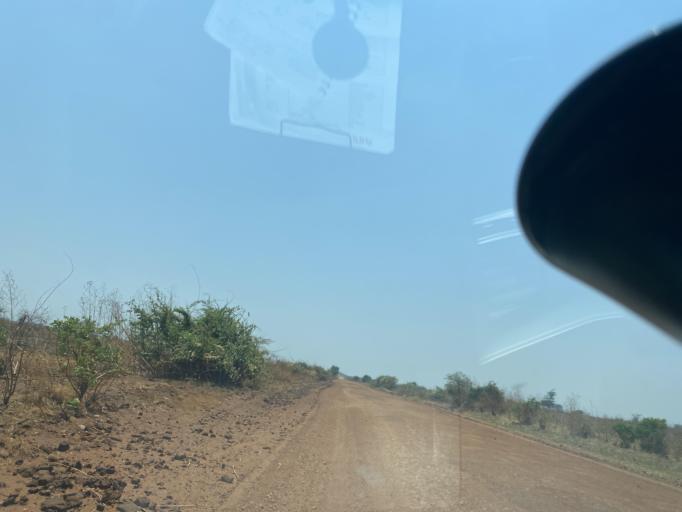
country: ZM
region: Lusaka
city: Lusaka
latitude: -15.4660
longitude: 27.9079
